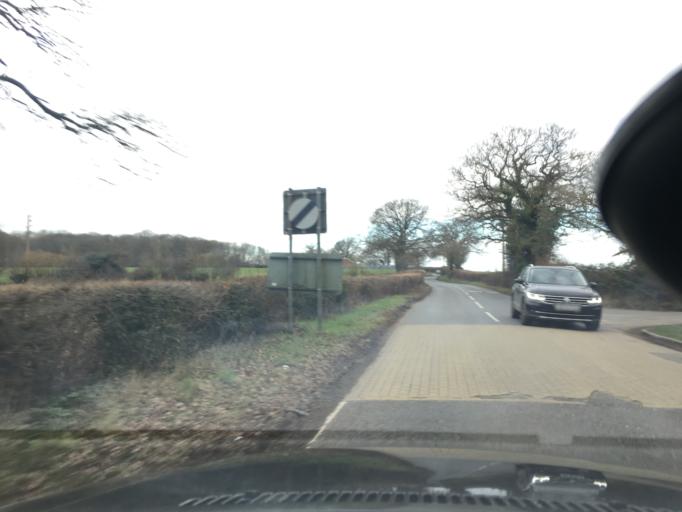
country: GB
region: England
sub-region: West Berkshire
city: Stratfield Mortimer
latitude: 51.3205
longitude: -1.0299
